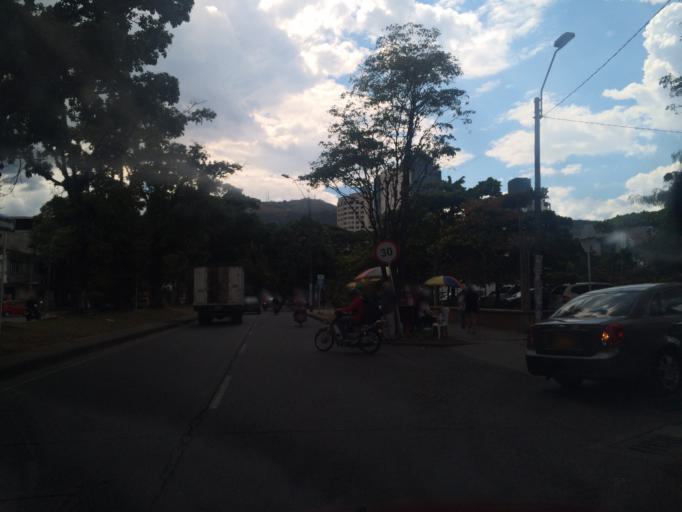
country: CO
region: Valle del Cauca
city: Cali
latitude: 3.4225
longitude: -76.5427
